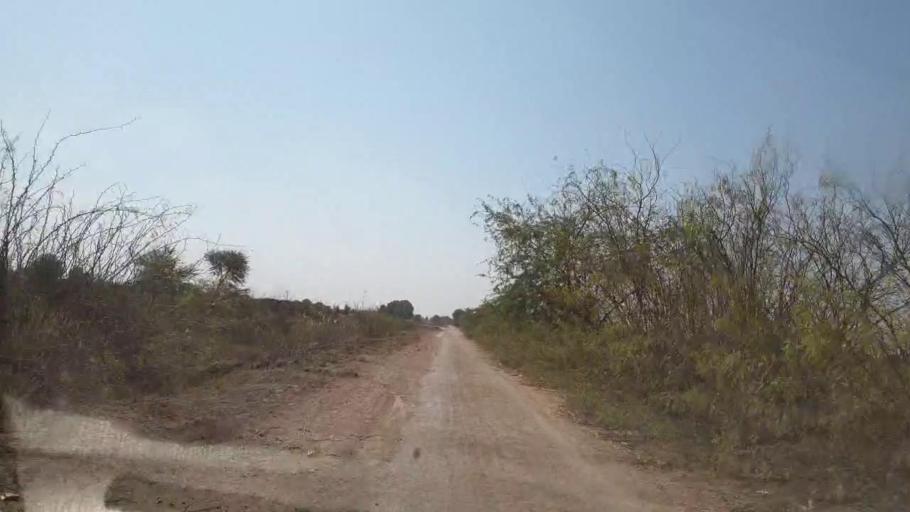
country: PK
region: Sindh
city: Mirpur Khas
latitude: 25.7216
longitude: 69.1058
